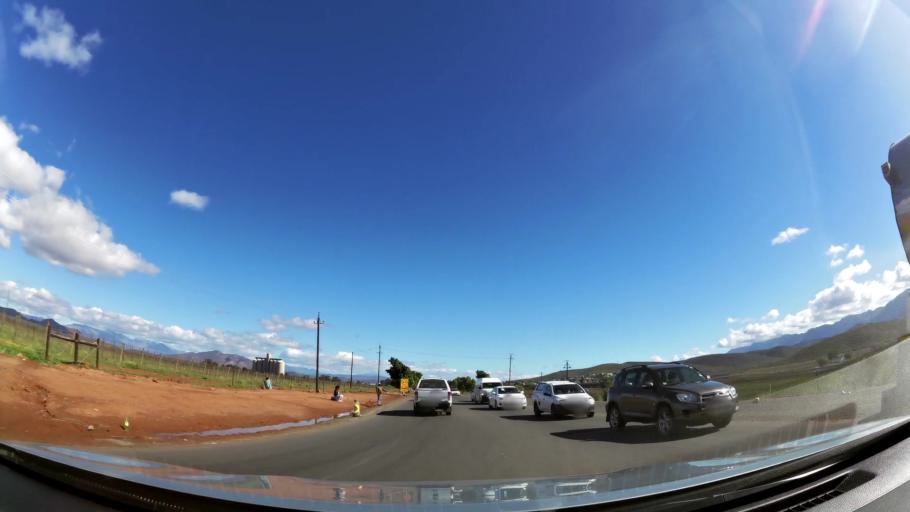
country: ZA
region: Western Cape
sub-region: Cape Winelands District Municipality
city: Ashton
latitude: -33.8308
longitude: 20.0805
